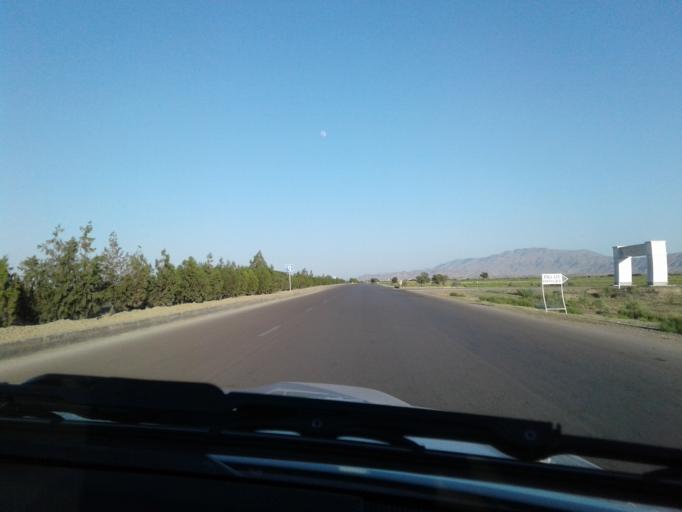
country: TM
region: Ahal
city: Baharly
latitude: 38.3500
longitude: 57.5490
